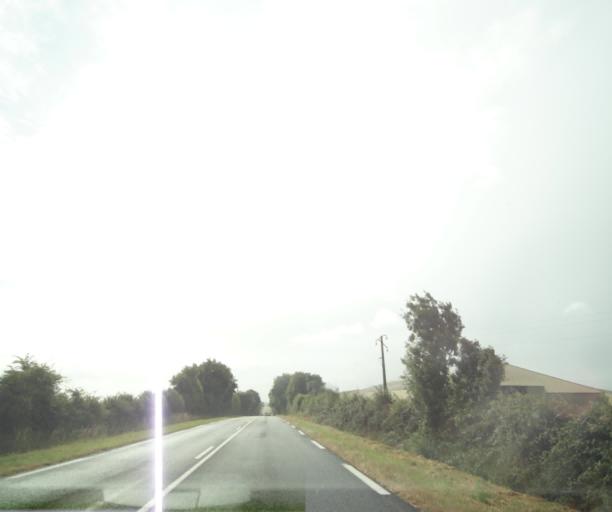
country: FR
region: Pays de la Loire
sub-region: Departement de la Vendee
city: Moutiers-les-Mauxfaits
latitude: 46.4571
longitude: -1.4328
